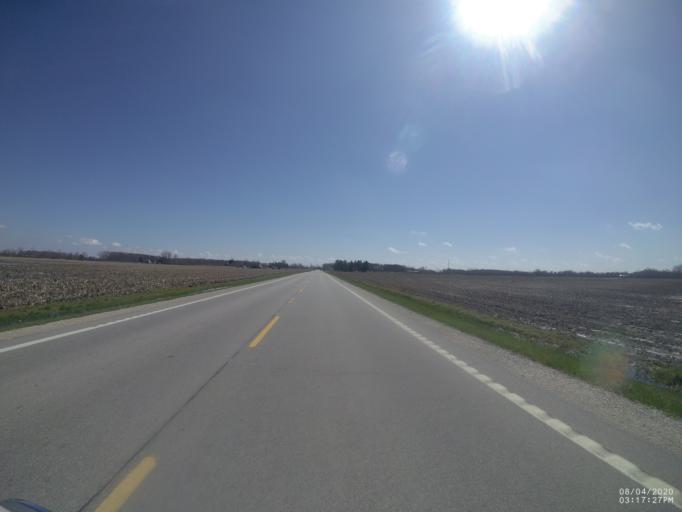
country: US
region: Ohio
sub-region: Sandusky County
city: Stony Prairie
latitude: 41.2747
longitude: -83.2353
